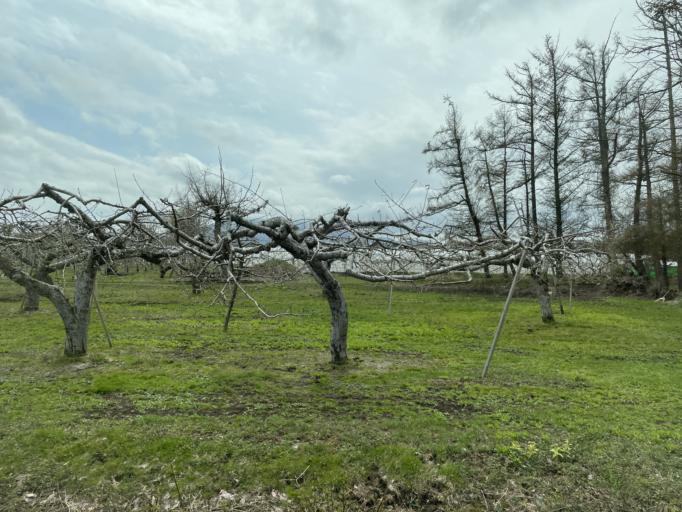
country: JP
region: Aomori
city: Shimokizukuri
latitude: 40.7867
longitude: 140.3036
